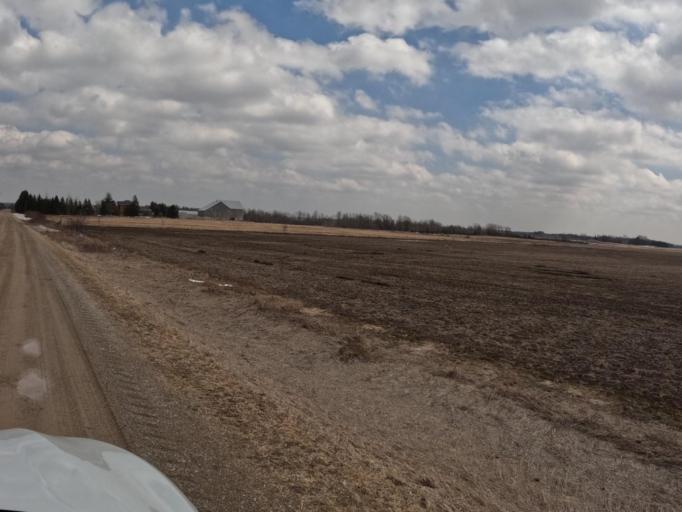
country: CA
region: Ontario
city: Shelburne
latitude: 44.0262
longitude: -80.2697
